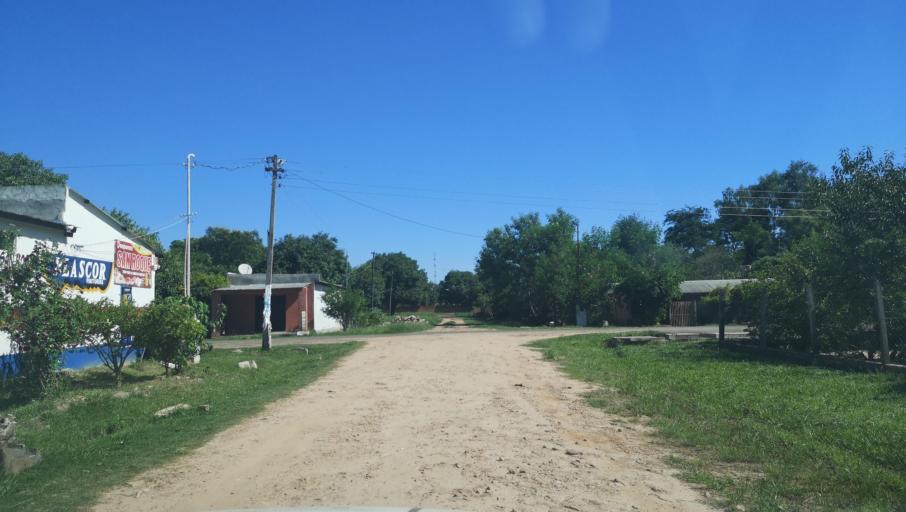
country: PY
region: Caaguazu
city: Carayao
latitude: -25.1982
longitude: -56.3942
